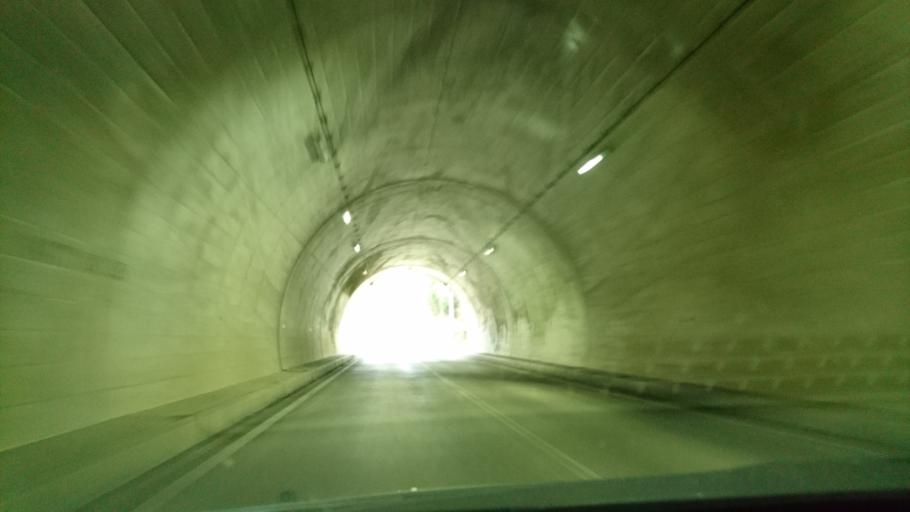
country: JP
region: Iwate
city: Ichinoseki
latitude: 38.9016
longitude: 140.9039
